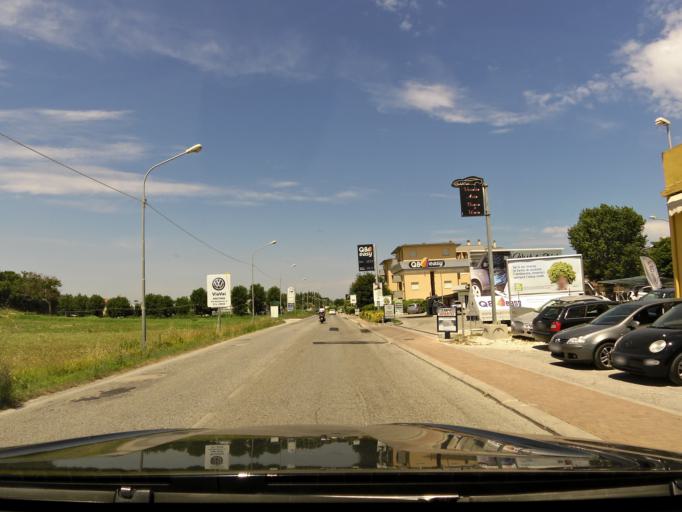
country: IT
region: The Marches
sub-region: Provincia di Pesaro e Urbino
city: Marotta
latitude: 43.7446
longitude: 13.1764
